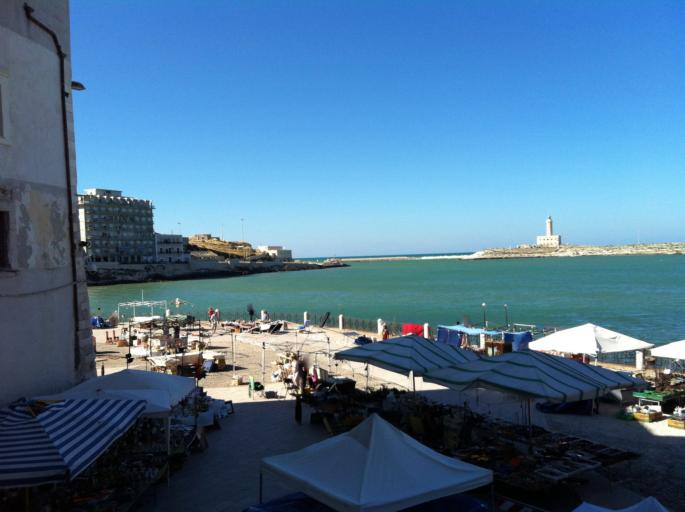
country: IT
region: Apulia
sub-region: Provincia di Foggia
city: Vieste
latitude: 41.8835
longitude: 16.1812
